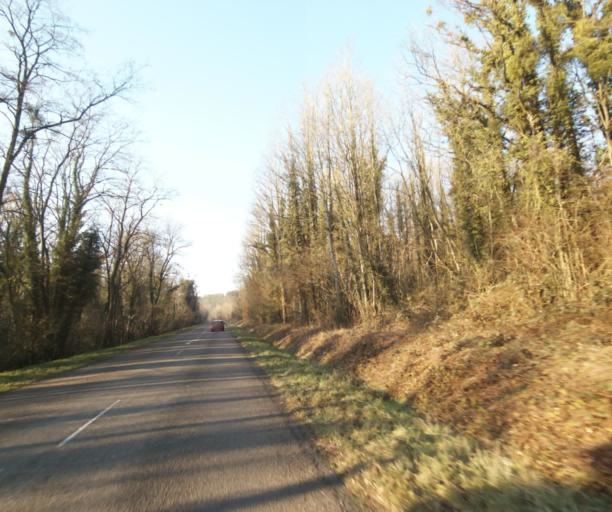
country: FR
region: Champagne-Ardenne
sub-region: Departement de la Haute-Marne
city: Bienville
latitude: 48.5619
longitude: 5.0660
